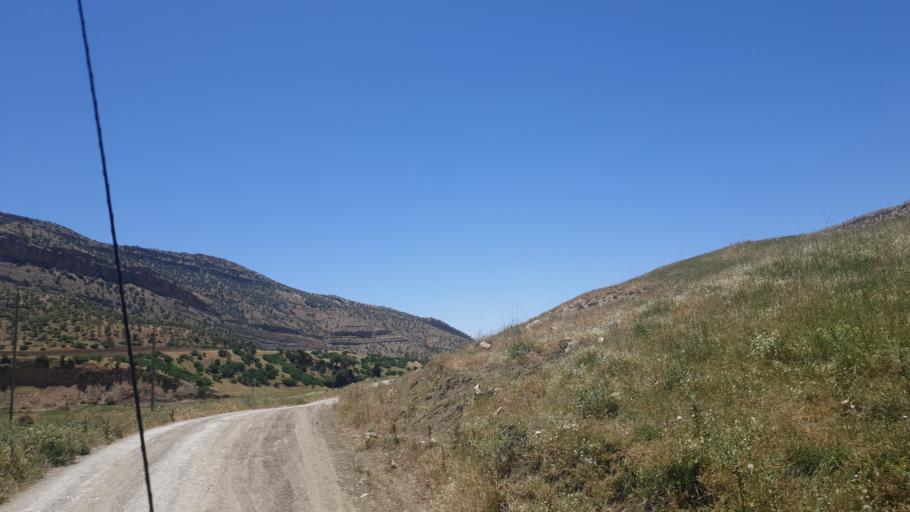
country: IQ
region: Arbil
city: Nahiyat Hiran
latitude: 36.1968
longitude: 44.4208
